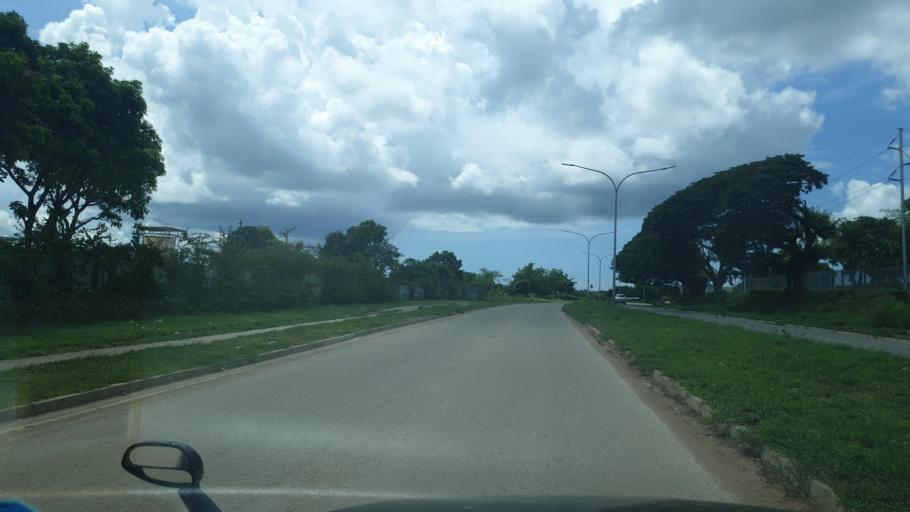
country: PG
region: National Capital
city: Port Moresby
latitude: -9.3803
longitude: 147.1555
